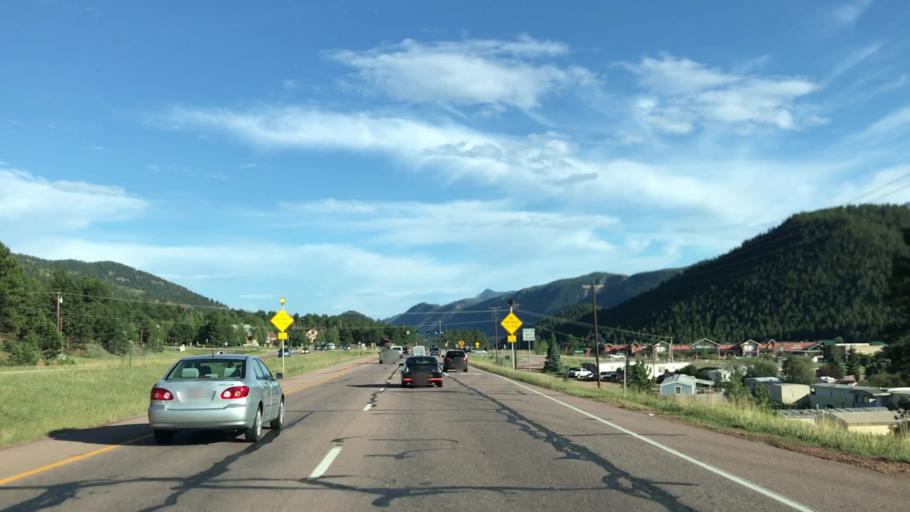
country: US
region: Colorado
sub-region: Teller County
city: Woodland Park
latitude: 38.9764
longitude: -105.0402
